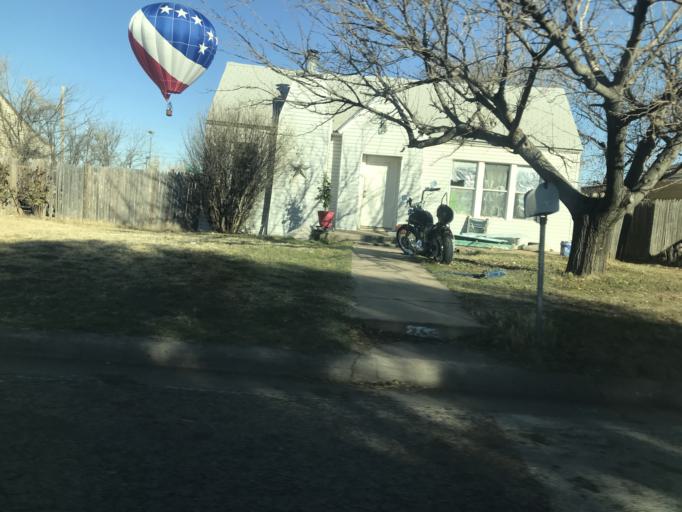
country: US
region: Texas
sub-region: Taylor County
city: Abilene
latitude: 32.4385
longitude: -99.7556
